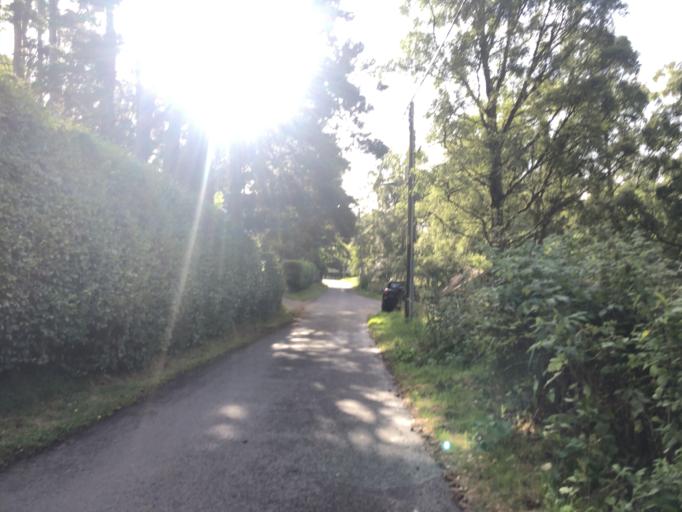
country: GB
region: Scotland
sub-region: Highland
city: Kingussie
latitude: 57.0663
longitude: -4.1279
